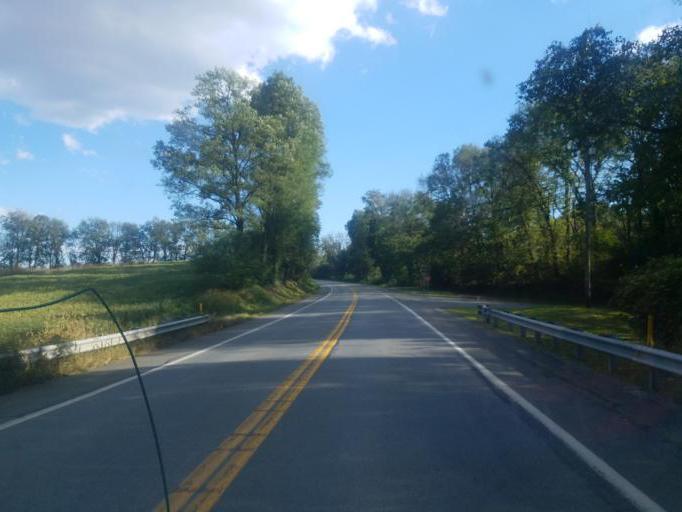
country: US
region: Pennsylvania
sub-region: Lancaster County
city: Bainbridge
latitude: 40.0817
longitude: -76.6576
